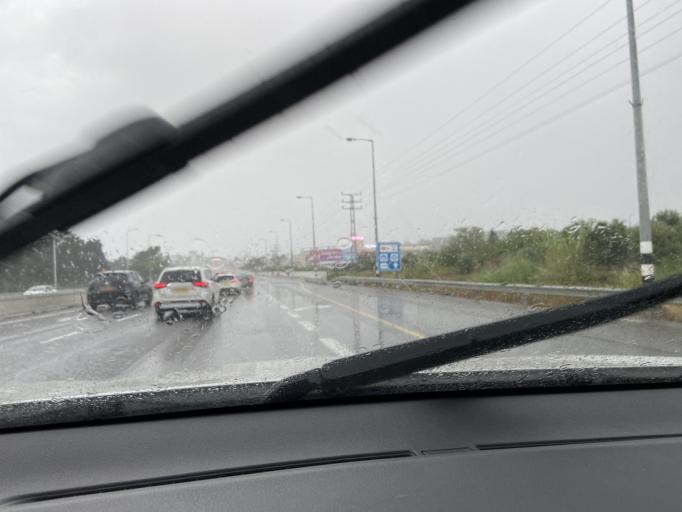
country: IL
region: Northern District
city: El Mazra`a
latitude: 32.9836
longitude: 35.0950
